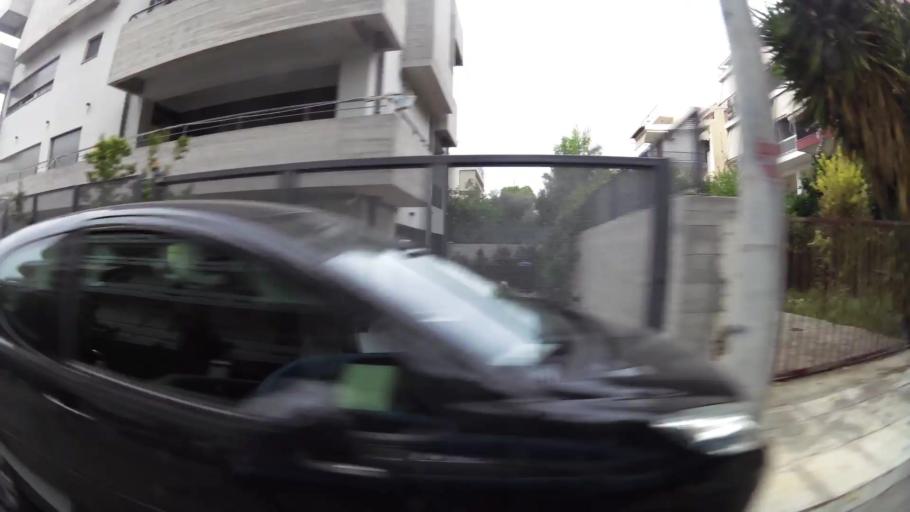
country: GR
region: Attica
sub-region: Nomarchia Athinas
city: Agios Dimitrios
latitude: 37.9217
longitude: 23.7411
